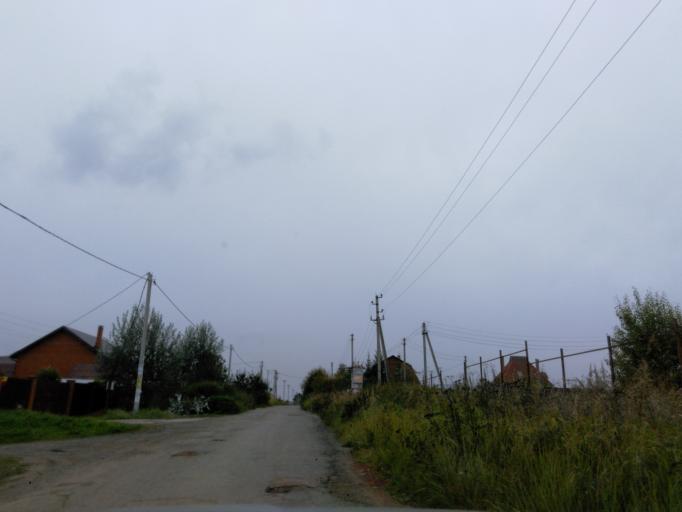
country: RU
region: Moskovskaya
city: Lozhki
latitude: 56.0645
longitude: 37.1017
